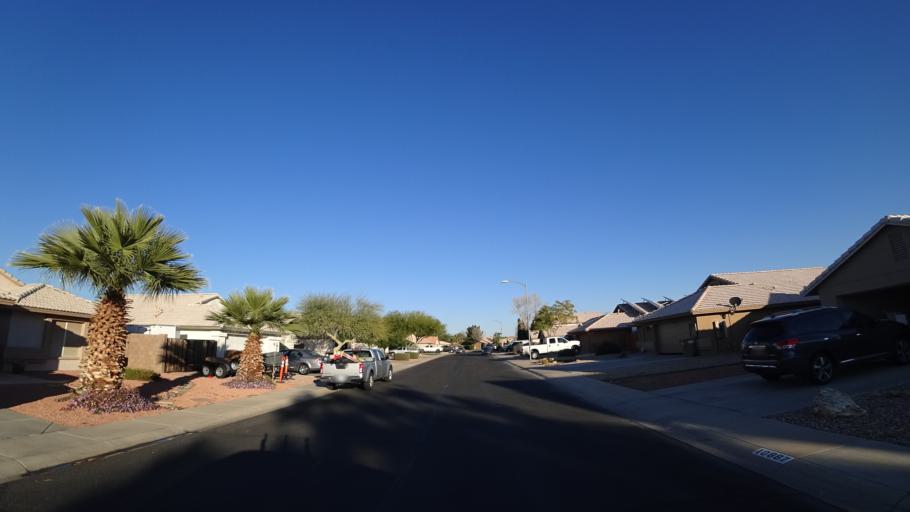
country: US
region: Arizona
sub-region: Maricopa County
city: Sun City West
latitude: 33.6804
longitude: -112.2939
